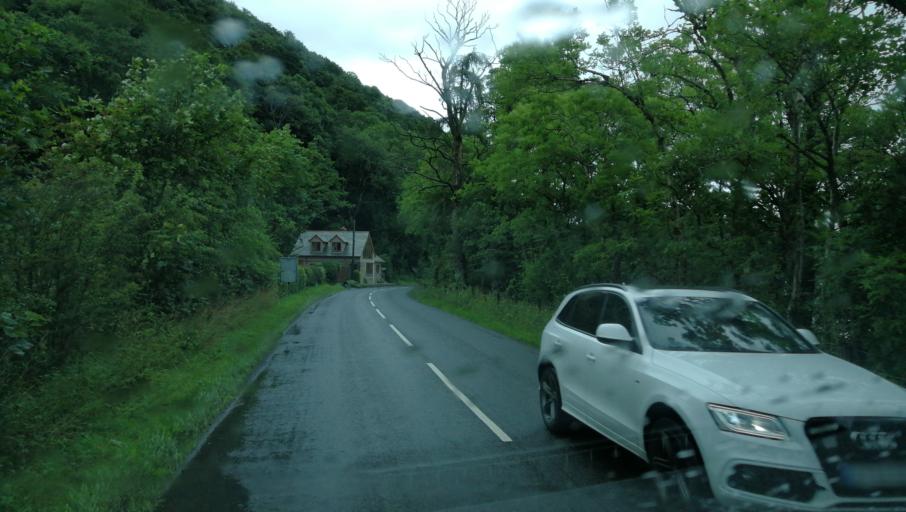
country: GB
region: England
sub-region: Cumbria
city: Penrith
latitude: 54.6062
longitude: -2.8399
